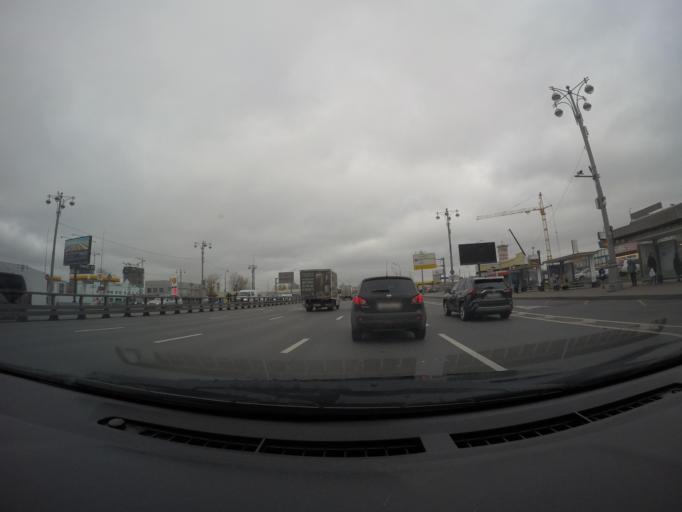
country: RU
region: Moscow
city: Mar'ina Roshcha
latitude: 55.7932
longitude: 37.6347
